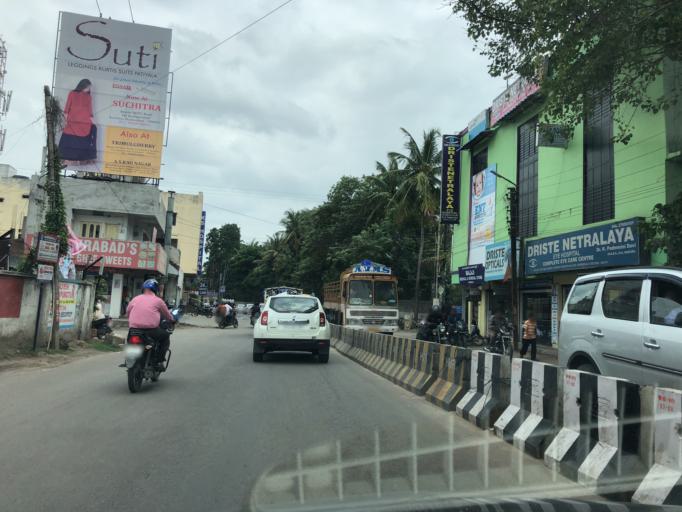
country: IN
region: Telangana
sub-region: Rangareddi
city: Quthbullapur
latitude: 17.4694
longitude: 78.4772
